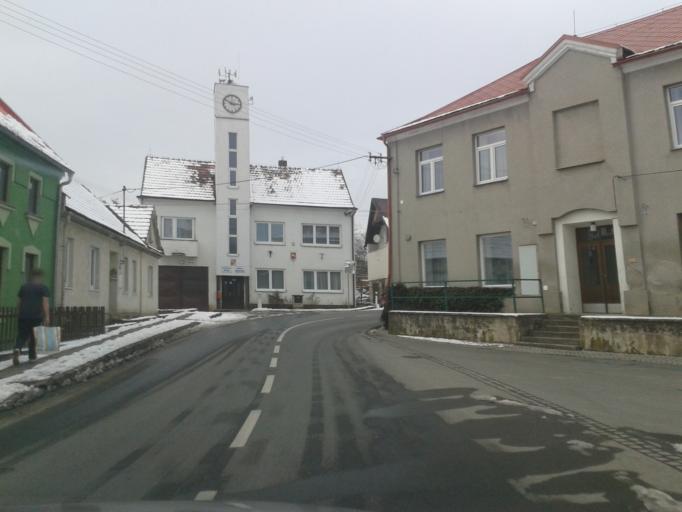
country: CZ
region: Olomoucky
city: Konice
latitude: 49.6079
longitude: 16.8923
